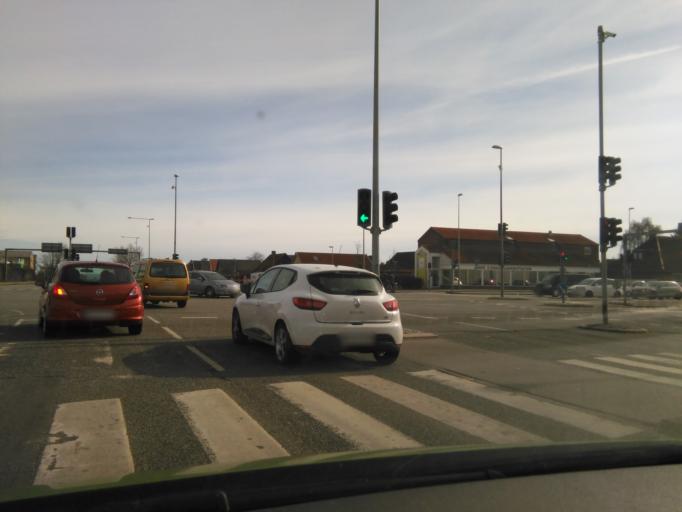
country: DK
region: Central Jutland
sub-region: Arhus Kommune
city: Arhus
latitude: 56.1824
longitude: 10.1969
